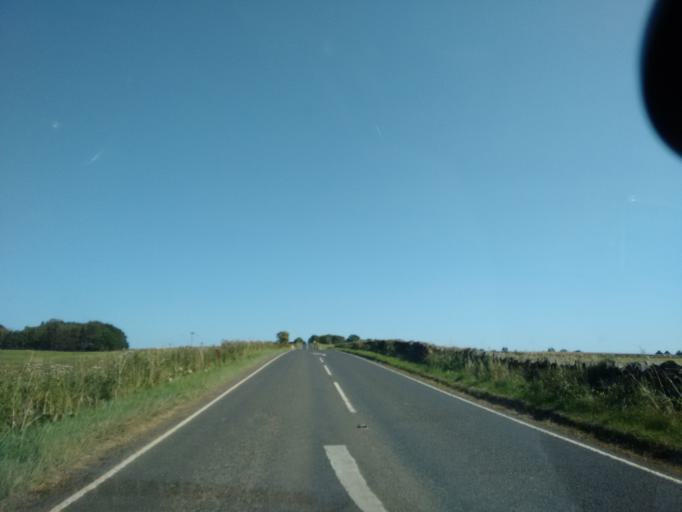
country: GB
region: England
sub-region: Northumberland
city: Acomb
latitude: 55.0186
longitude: -2.0691
